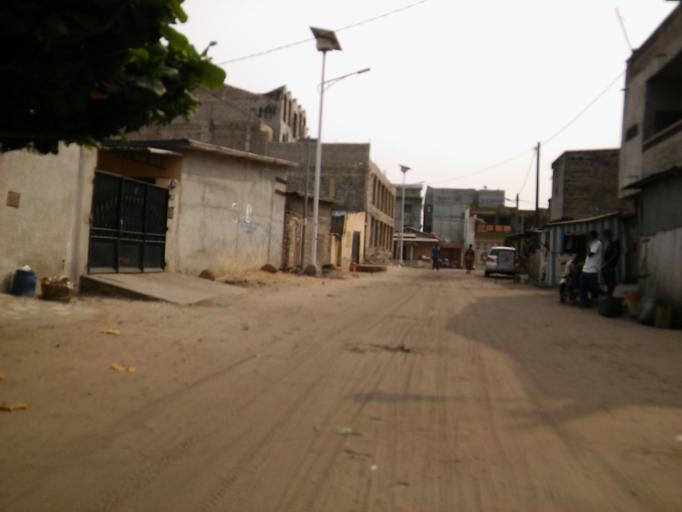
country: BJ
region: Littoral
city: Cotonou
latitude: 6.3935
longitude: 2.3779
